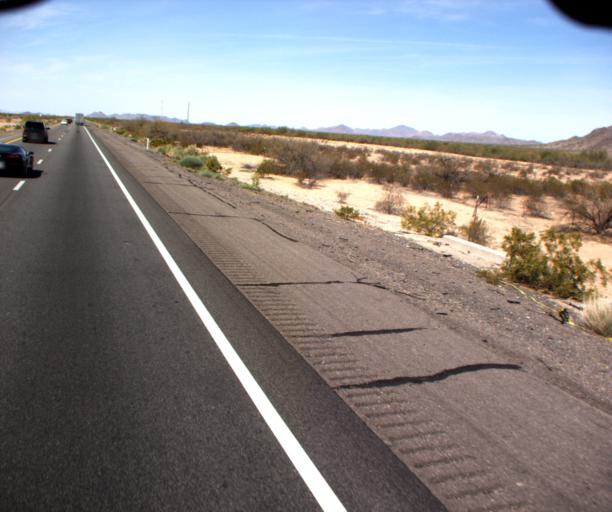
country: US
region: Arizona
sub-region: La Paz County
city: Salome
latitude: 33.5839
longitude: -113.4495
